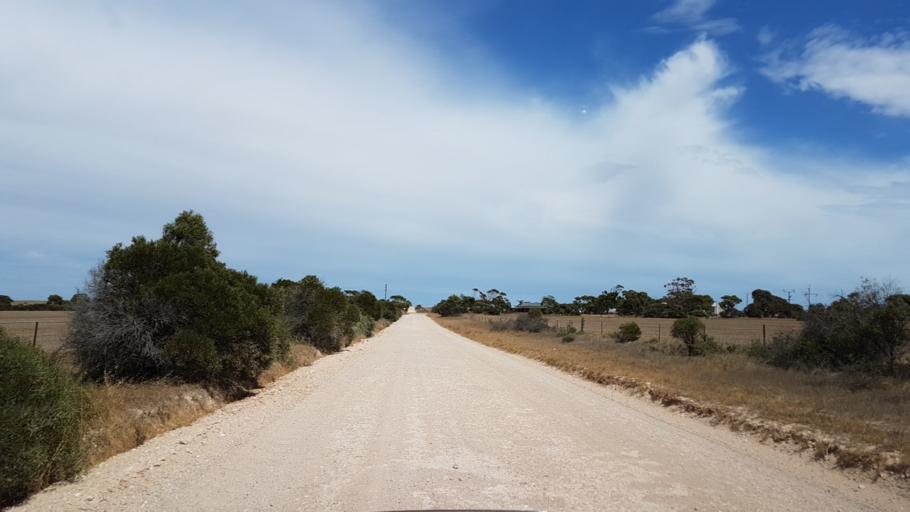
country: AU
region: South Australia
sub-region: Yorke Peninsula
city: Ardrossan
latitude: -34.3991
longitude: 137.9198
